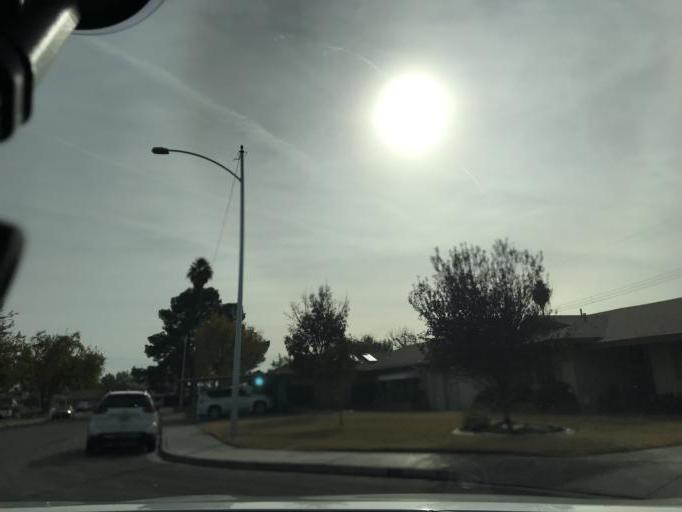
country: US
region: Nevada
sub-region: Clark County
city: Las Vegas
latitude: 36.1752
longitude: -115.1670
